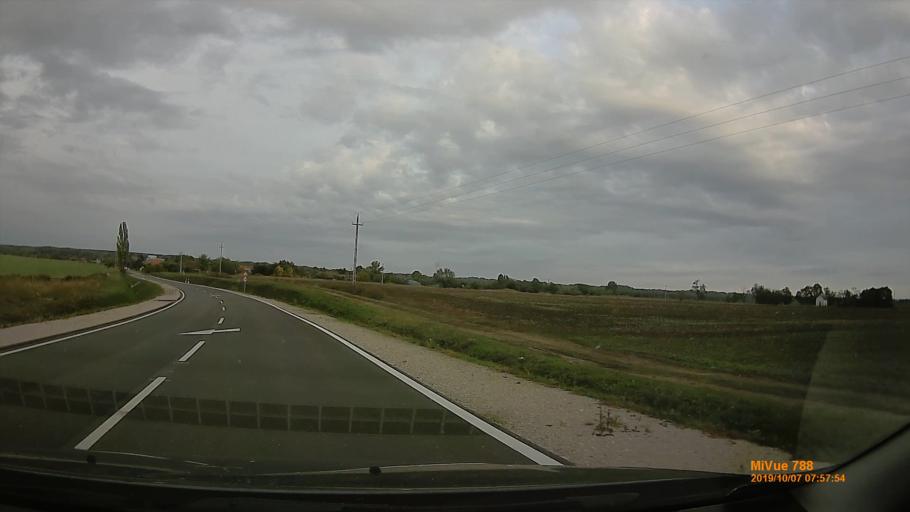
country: HU
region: Jasz-Nagykun-Szolnok
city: Cserkeszolo
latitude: 46.8816
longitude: 20.1393
